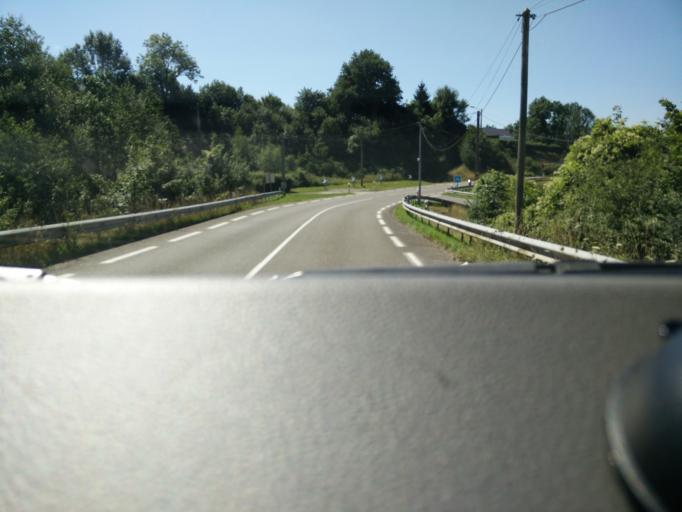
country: FR
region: Nord-Pas-de-Calais
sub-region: Departement du Nord
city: Trelon
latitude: 50.1262
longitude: 4.0828
